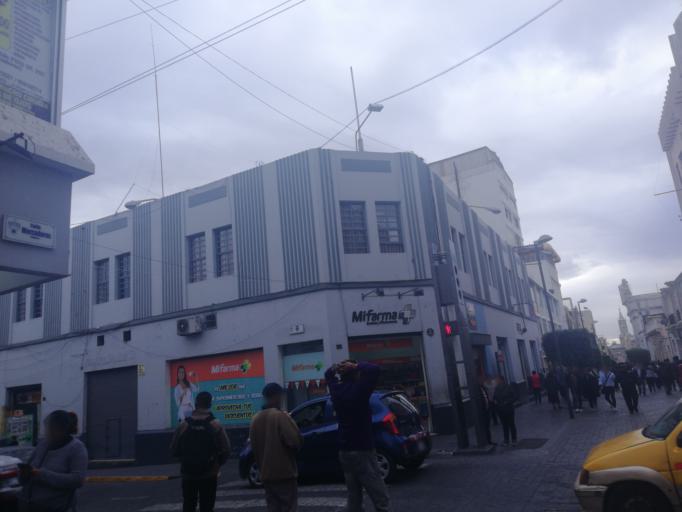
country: PE
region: Arequipa
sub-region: Provincia de Arequipa
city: Arequipa
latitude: -16.3997
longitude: -71.5329
